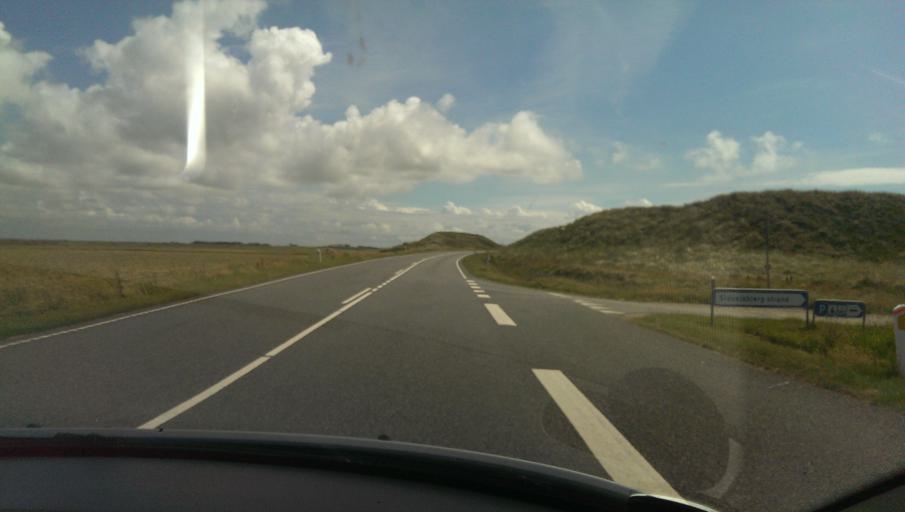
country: DK
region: Central Jutland
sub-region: Ringkobing-Skjern Kommune
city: Ringkobing
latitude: 56.1753
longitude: 8.1284
